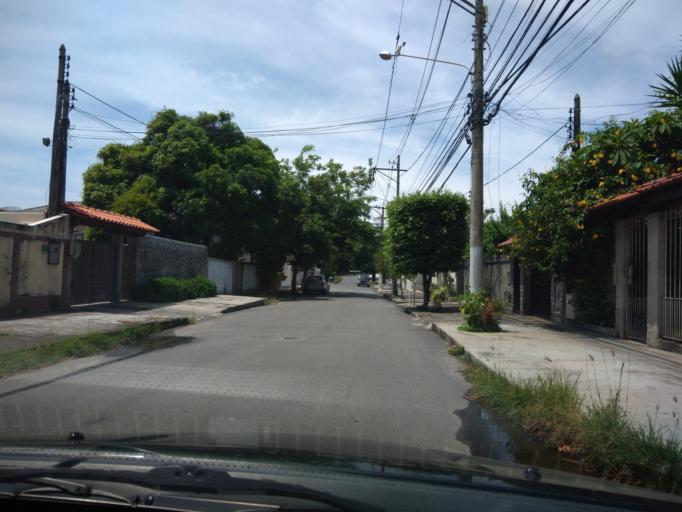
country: BR
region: Rio de Janeiro
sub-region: Niteroi
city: Niteroi
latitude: -22.9363
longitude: -43.0668
